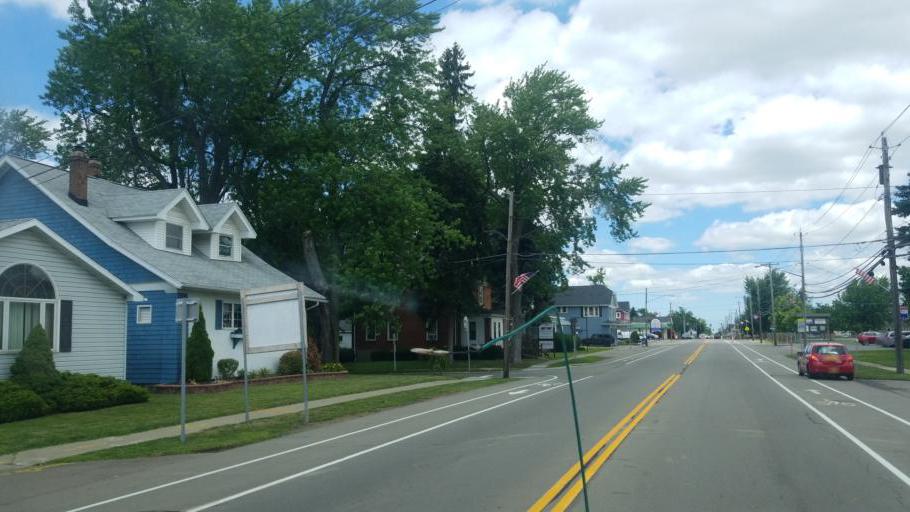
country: US
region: New York
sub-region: Erie County
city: Blasdell
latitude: 42.7931
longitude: -78.8238
